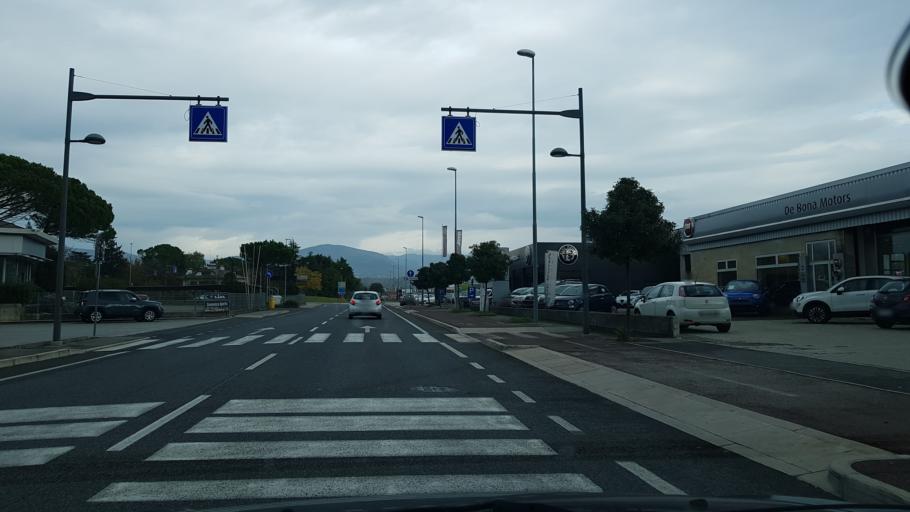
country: IT
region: Friuli Venezia Giulia
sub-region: Provincia di Gorizia
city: Gorizia
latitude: 45.9249
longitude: 13.6171
